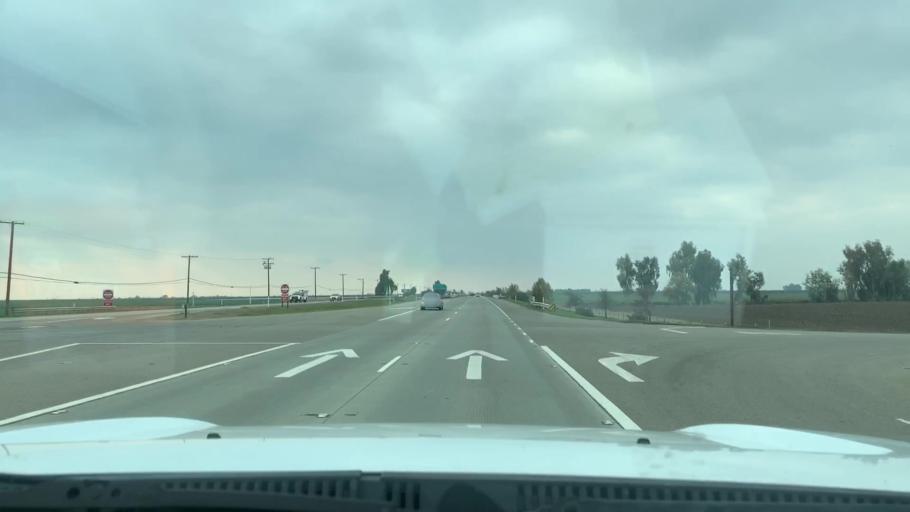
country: US
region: California
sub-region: Kings County
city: Home Garden
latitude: 36.3287
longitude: -119.5291
